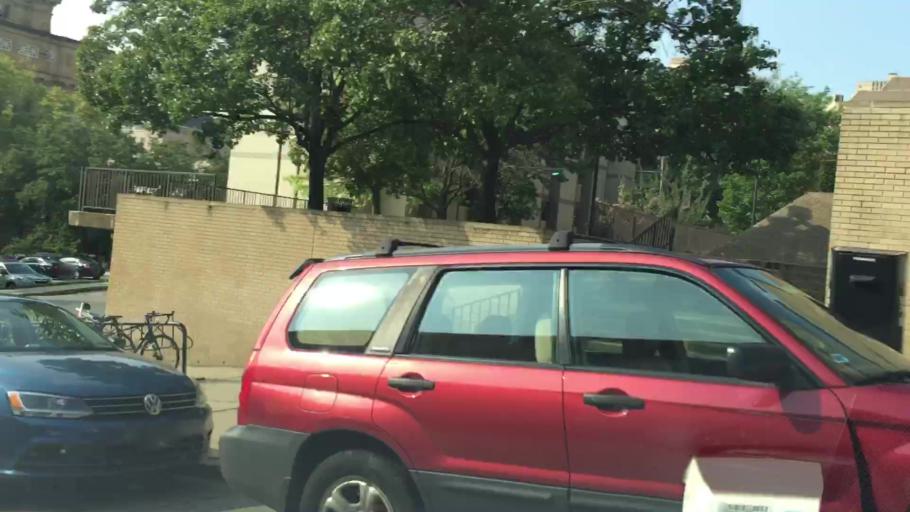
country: US
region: Pennsylvania
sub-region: Allegheny County
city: Bloomfield
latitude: 40.4461
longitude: -79.9569
